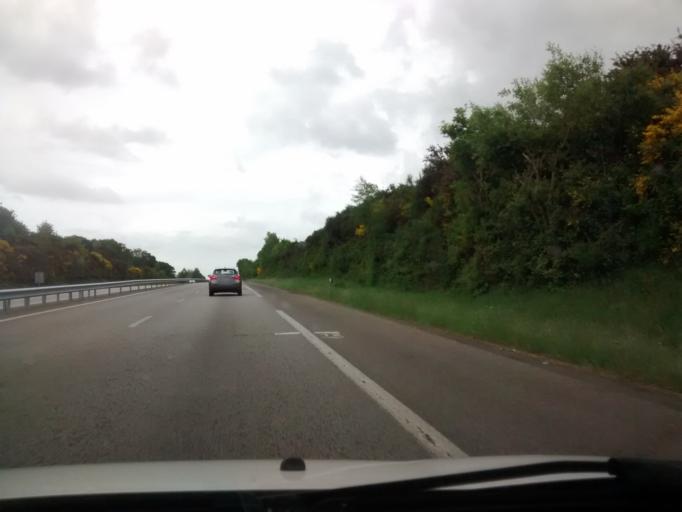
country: FR
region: Brittany
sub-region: Departement du Morbihan
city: Augan
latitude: 47.9296
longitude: -2.2456
